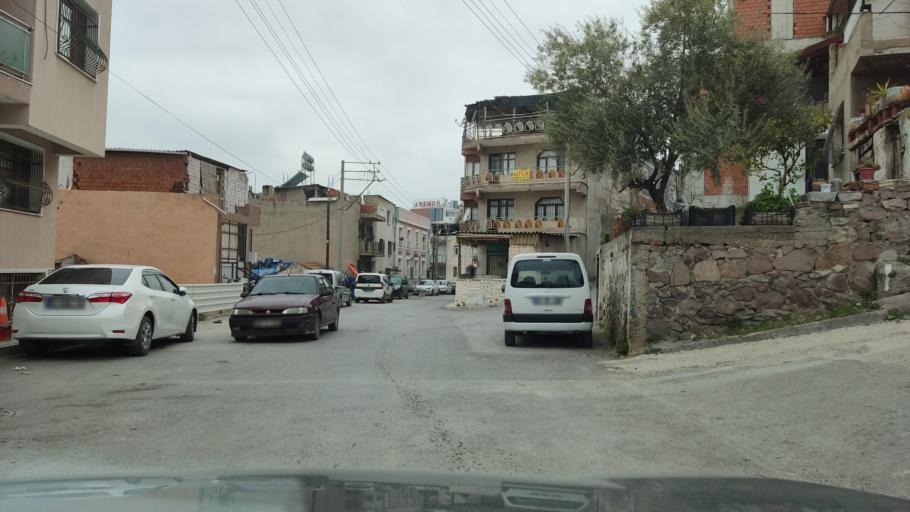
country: TR
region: Izmir
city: Karsiyaka
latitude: 38.4916
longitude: 27.0685
